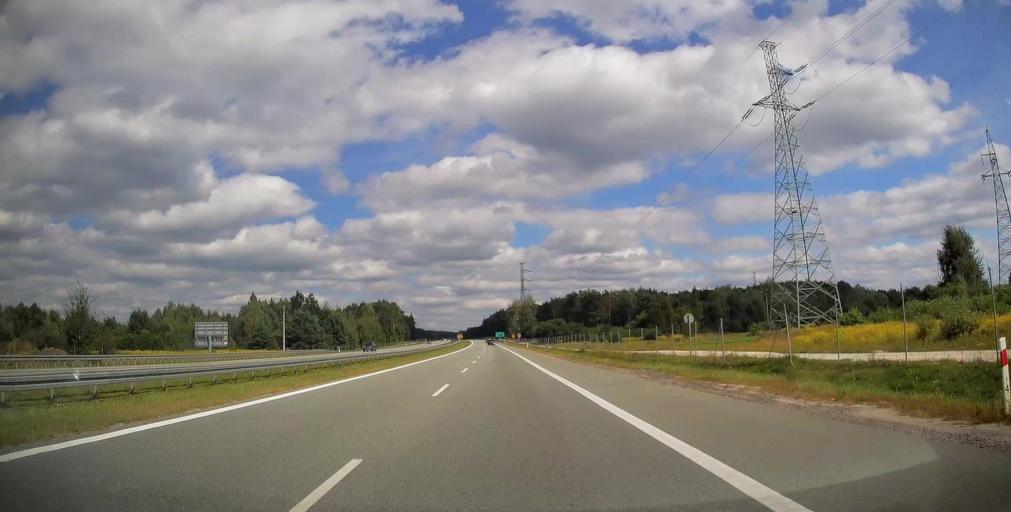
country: PL
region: Swietokrzyskie
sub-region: Powiat kielecki
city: Kostomloty Pierwsze
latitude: 50.9114
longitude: 20.5944
